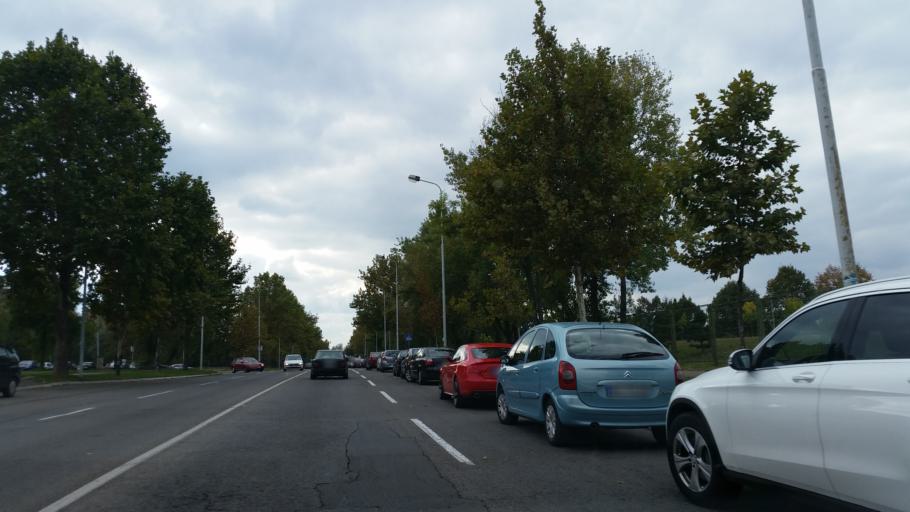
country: RS
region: Central Serbia
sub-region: Belgrade
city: Zemun
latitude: 44.8196
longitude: 20.3727
